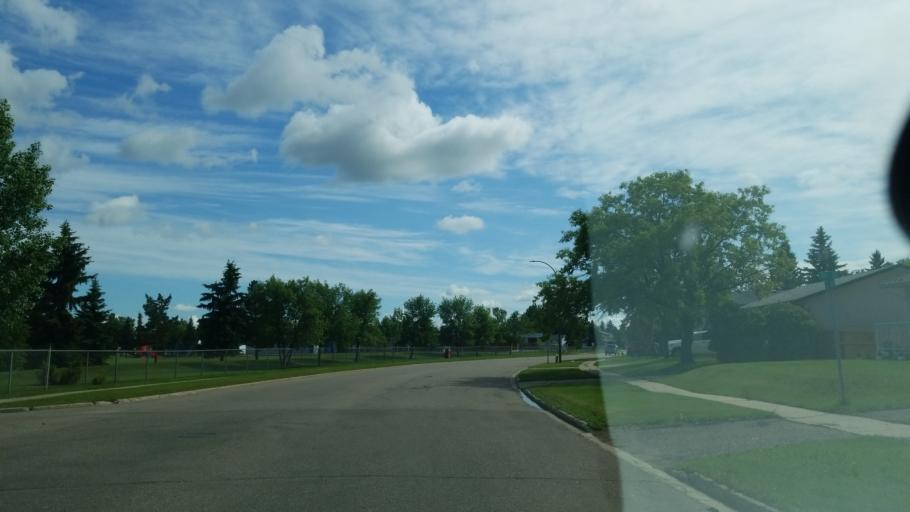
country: CA
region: Saskatchewan
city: Lloydminster
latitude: 53.2683
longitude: -110.0117
